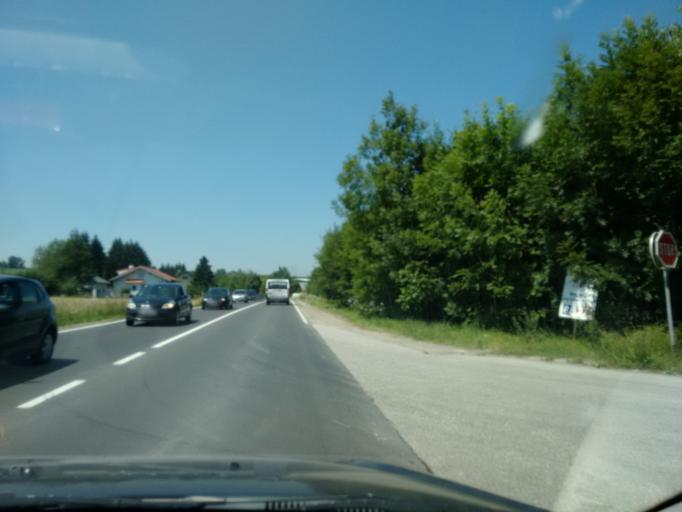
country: AT
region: Upper Austria
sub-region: Politischer Bezirk Gmunden
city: Altmunster
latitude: 47.9540
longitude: 13.7443
